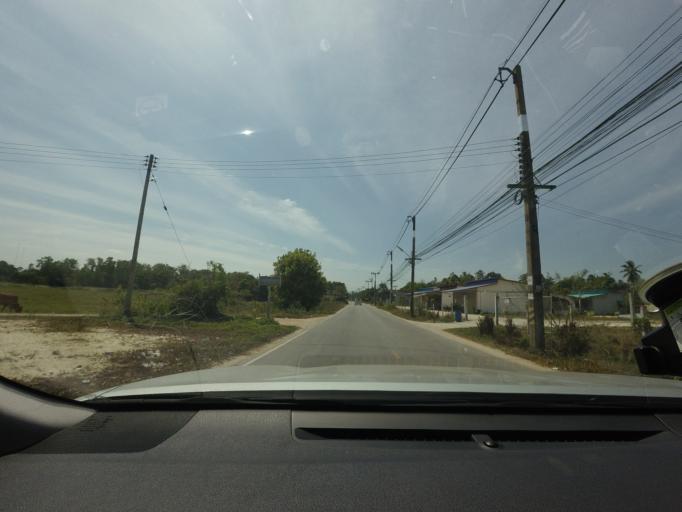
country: TH
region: Narathiwat
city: Narathiwat
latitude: 6.4441
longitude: 101.8036
